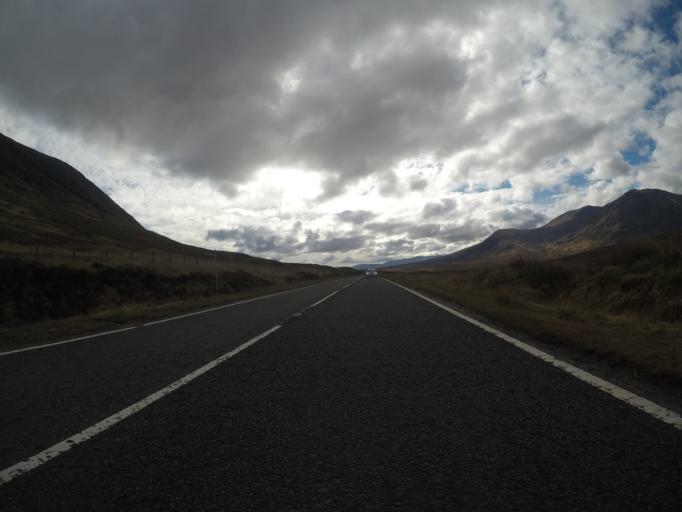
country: GB
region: Scotland
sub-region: Highland
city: Spean Bridge
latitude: 56.6599
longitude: -4.8859
